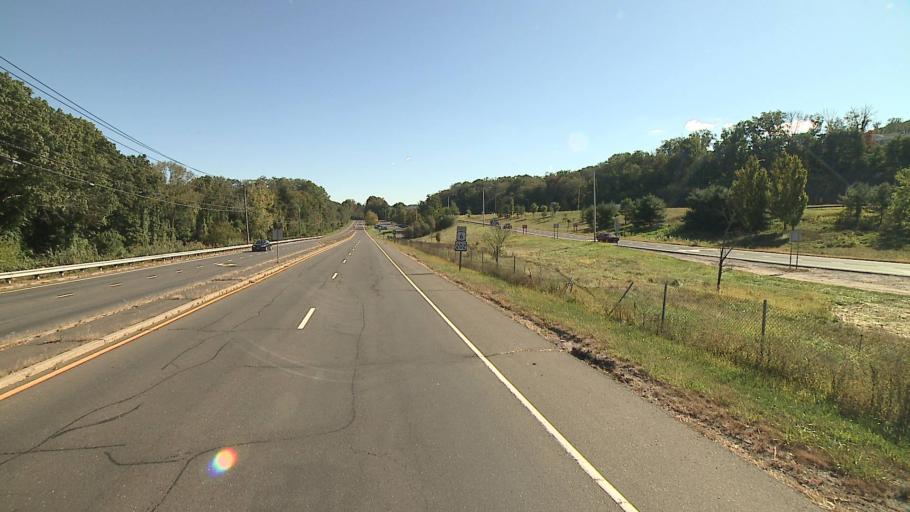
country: US
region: New York
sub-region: Putnam County
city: Peach Lake
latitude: 41.3908
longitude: -73.5403
